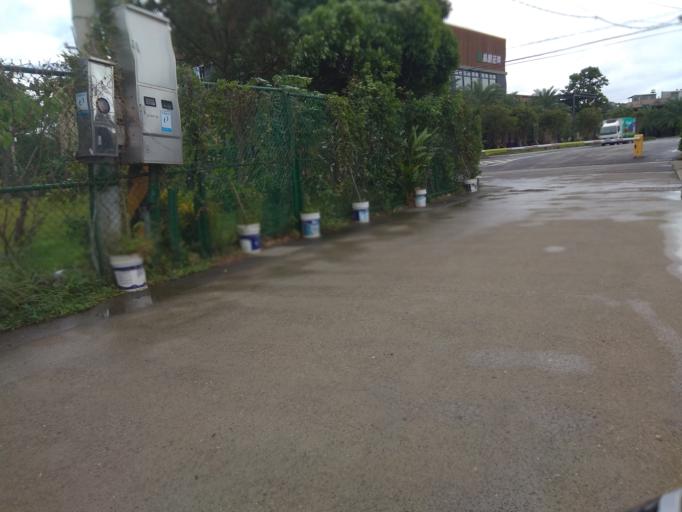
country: TW
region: Taiwan
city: Daxi
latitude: 24.9439
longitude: 121.1905
